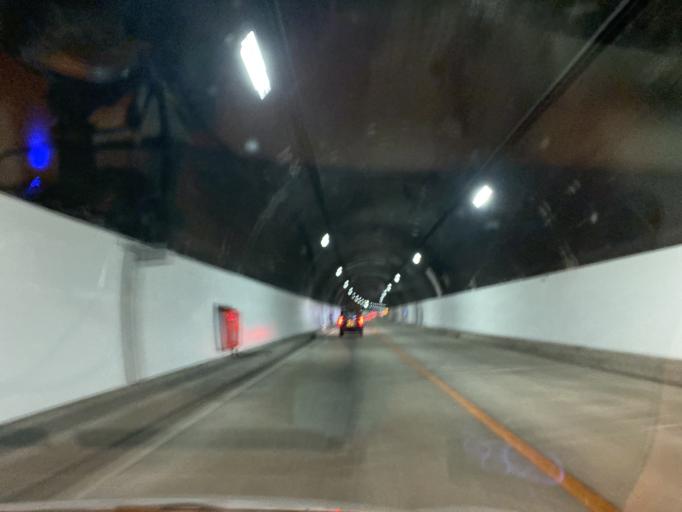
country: JP
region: Wakayama
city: Iwade
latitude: 34.3513
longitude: 135.2889
